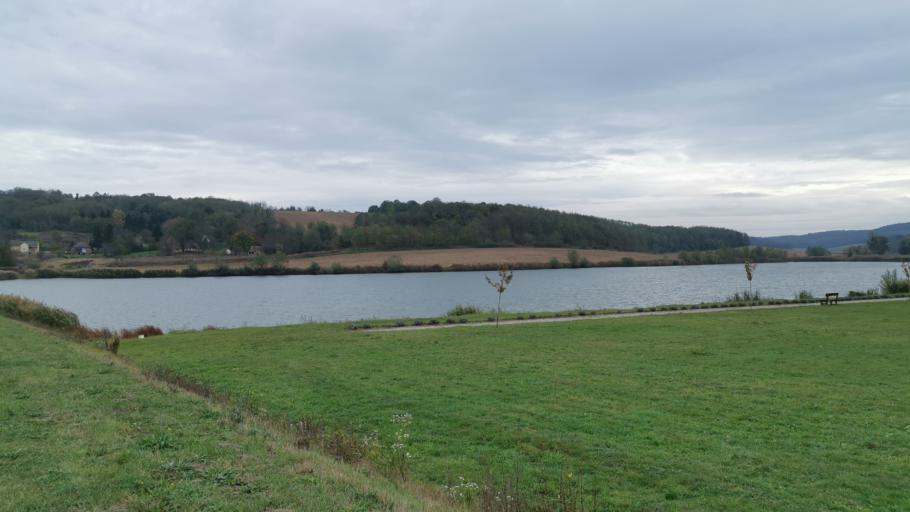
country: HU
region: Somogy
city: Kaposmero
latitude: 46.2718
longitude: 17.7258
